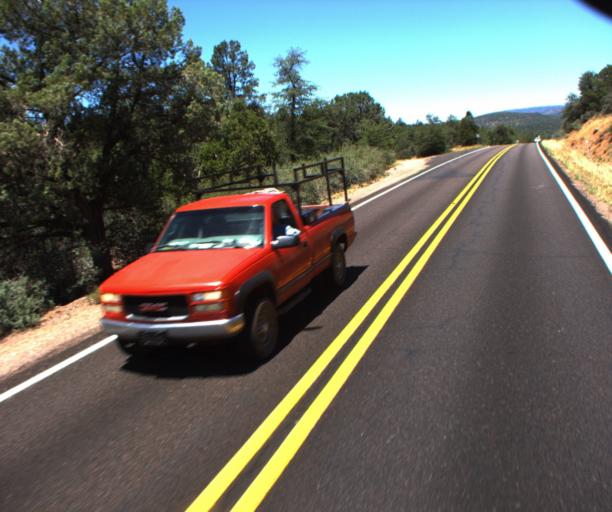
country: US
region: Arizona
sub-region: Gila County
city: Payson
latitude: 34.2882
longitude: -111.3424
